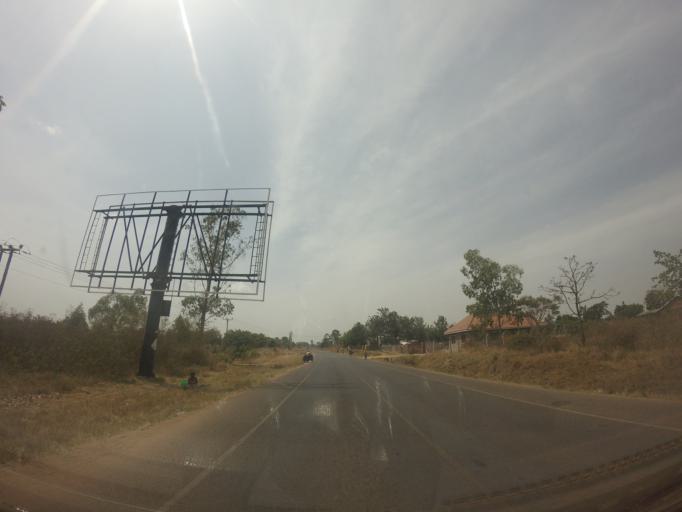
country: UG
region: Northern Region
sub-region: Arua District
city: Arua
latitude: 2.9690
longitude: 30.9187
